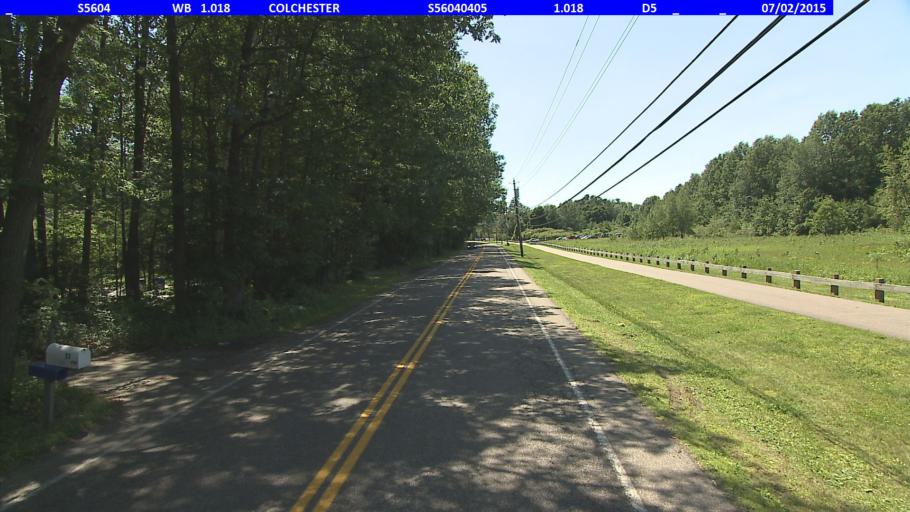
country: US
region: Vermont
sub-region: Chittenden County
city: Burlington
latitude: 44.5509
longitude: -73.2506
